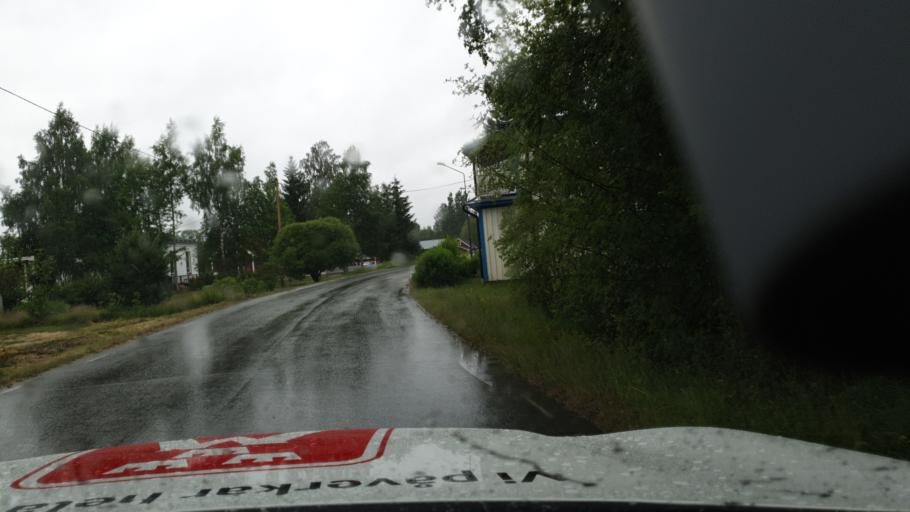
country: SE
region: Vaesterbotten
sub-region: Nordmalings Kommun
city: Nordmaling
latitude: 63.5474
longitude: 19.3965
